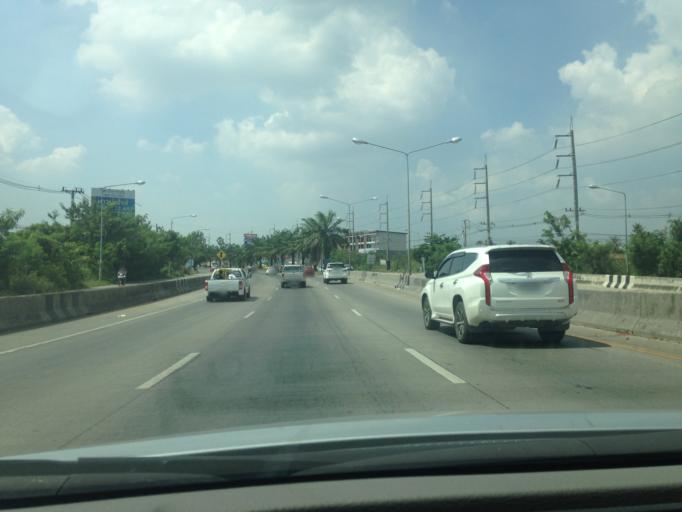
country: TH
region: Pathum Thani
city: Pathum Thani
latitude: 14.0273
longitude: 100.5375
